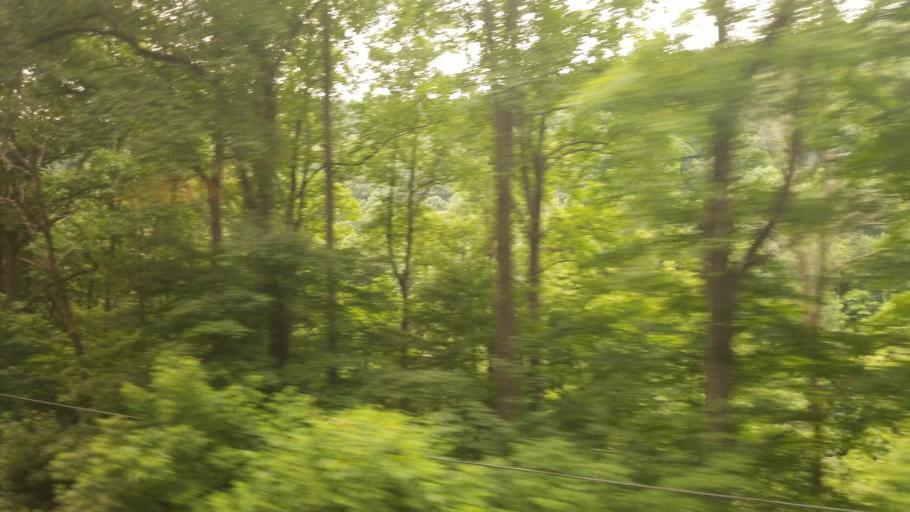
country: US
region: Pennsylvania
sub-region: Fayette County
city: South Connellsville
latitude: 39.9120
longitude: -79.4800
